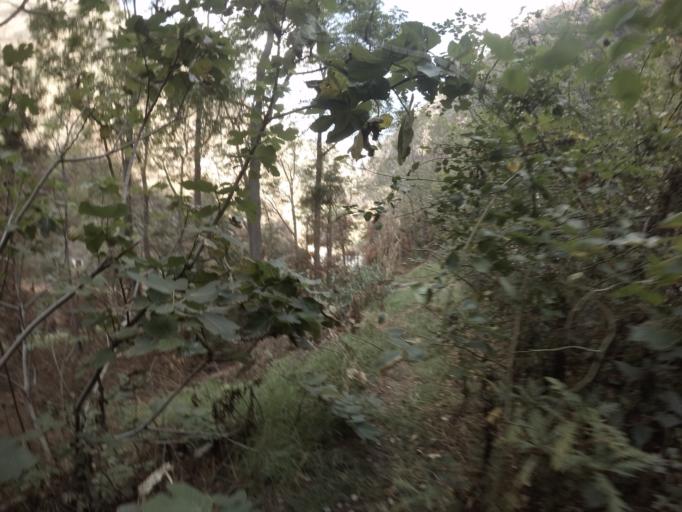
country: PT
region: Madeira
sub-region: Funchal
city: Nossa Senhora do Monte
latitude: 32.6934
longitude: -16.9161
